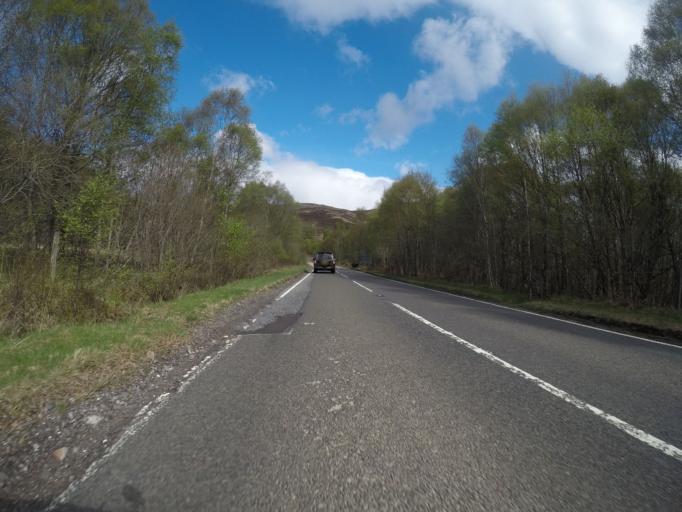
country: GB
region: Scotland
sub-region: Highland
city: Spean Bridge
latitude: 57.1447
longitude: -4.9582
